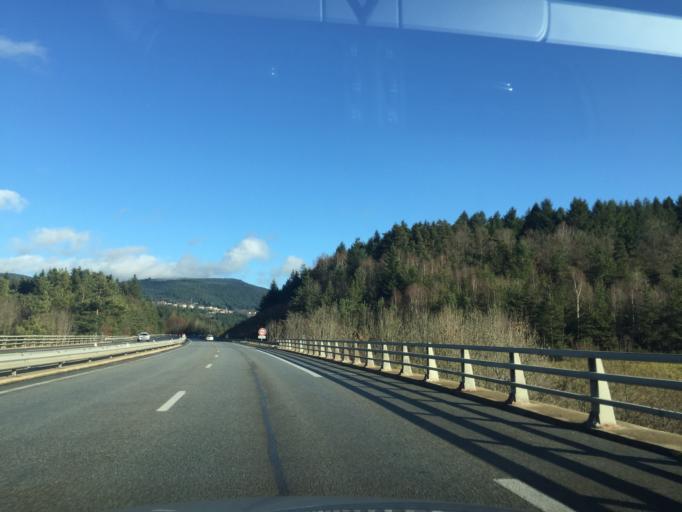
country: FR
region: Auvergne
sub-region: Departement du Puy-de-Dome
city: Chabreloche
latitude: 45.8748
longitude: 3.6796
